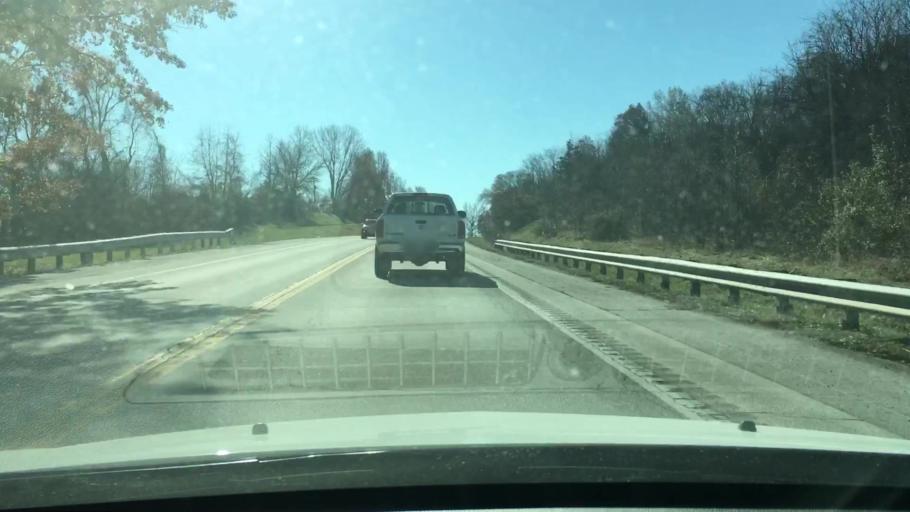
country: US
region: Missouri
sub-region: Pike County
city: Louisiana
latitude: 39.4345
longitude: -91.0801
